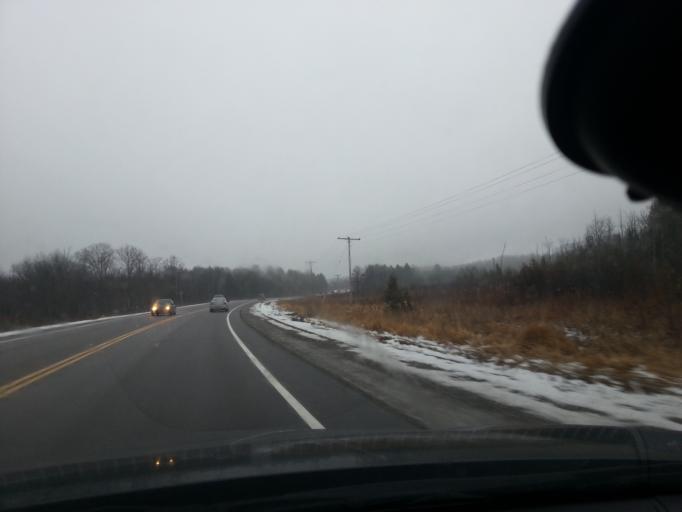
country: CA
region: Ontario
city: Skatepark
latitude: 44.7545
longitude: -76.8932
